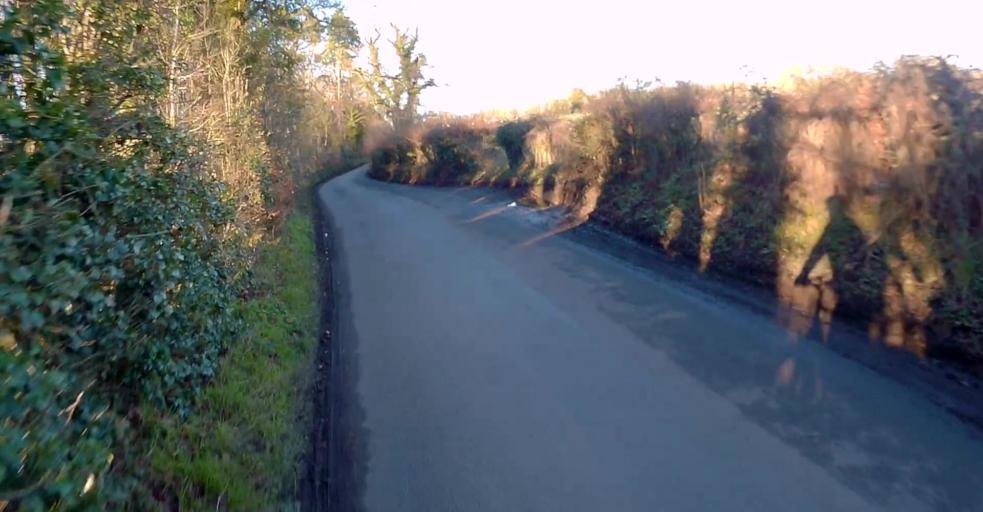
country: GB
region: England
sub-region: Hampshire
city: Hook
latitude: 51.2969
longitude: -0.9821
